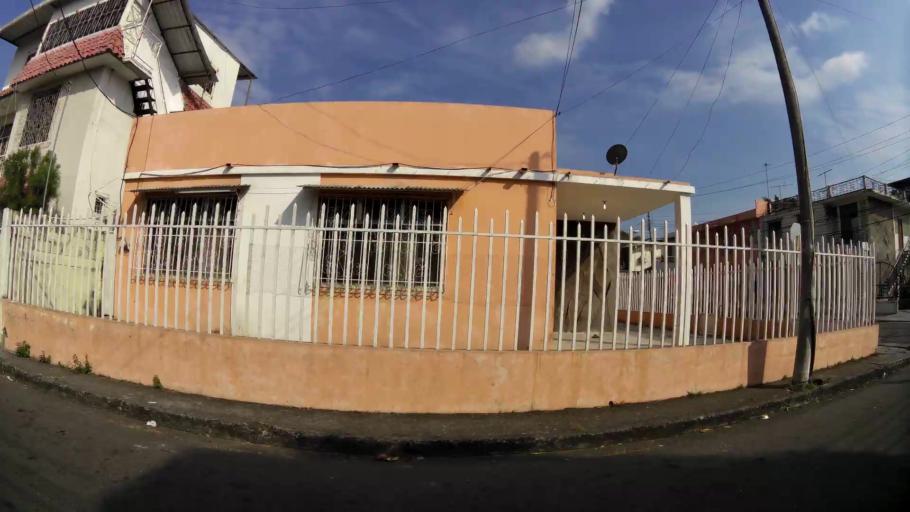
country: EC
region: Guayas
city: Guayaquil
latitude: -2.1877
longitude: -79.9019
